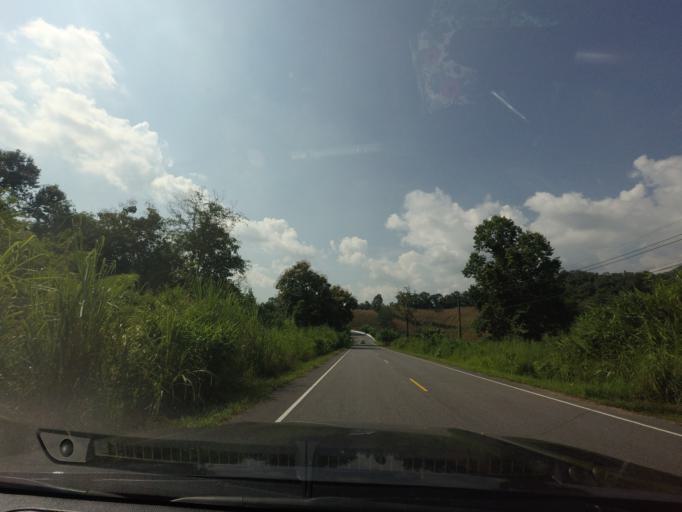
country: TH
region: Nan
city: Santi Suk
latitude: 18.9817
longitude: 100.9996
